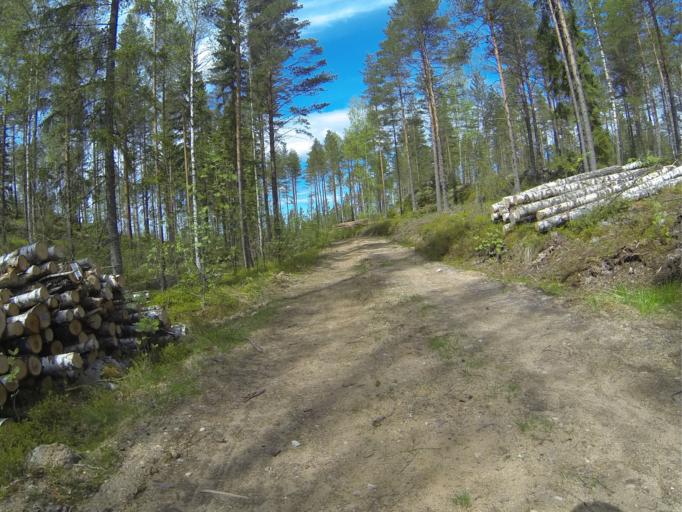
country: FI
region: Varsinais-Suomi
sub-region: Salo
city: Halikko
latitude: 60.3316
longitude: 23.0741
